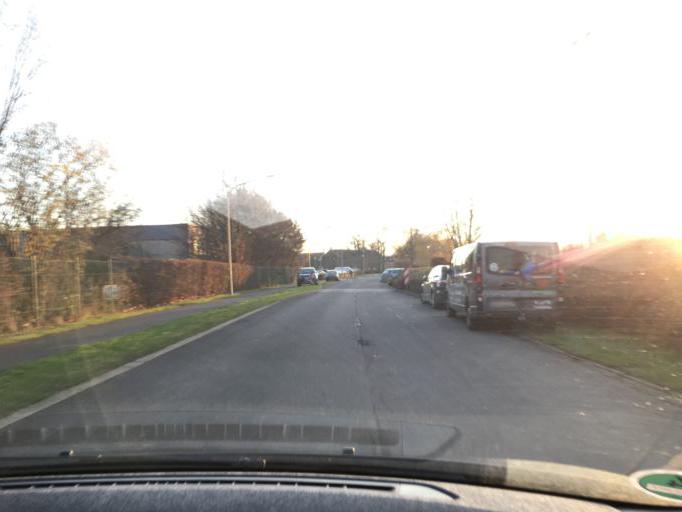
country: DE
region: North Rhine-Westphalia
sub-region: Regierungsbezirk Koln
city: Inden
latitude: 50.8523
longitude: 6.3599
